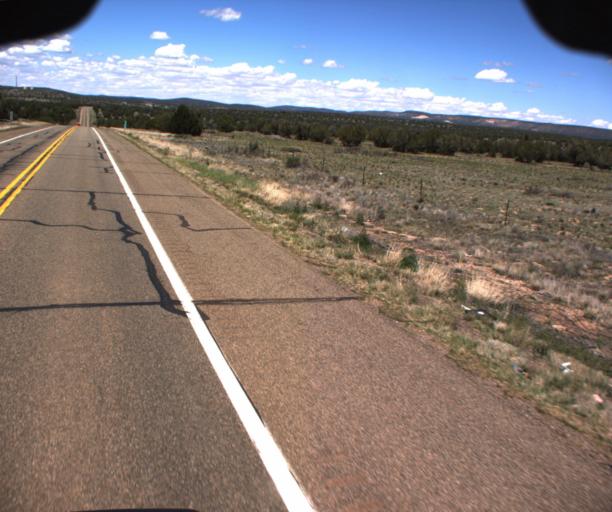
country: US
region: Arizona
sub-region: Coconino County
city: Williams
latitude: 35.1946
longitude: -112.4713
